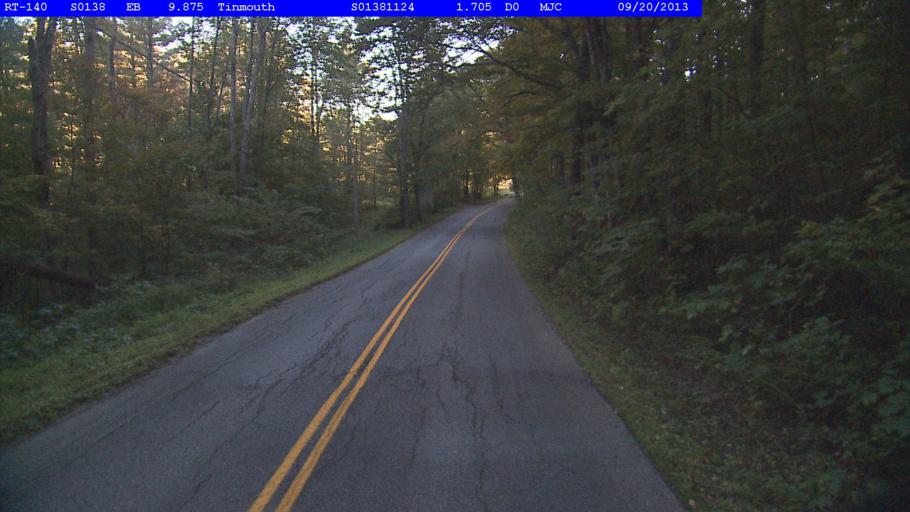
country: US
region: Vermont
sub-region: Rutland County
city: West Rutland
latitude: 43.4700
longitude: -73.0501
